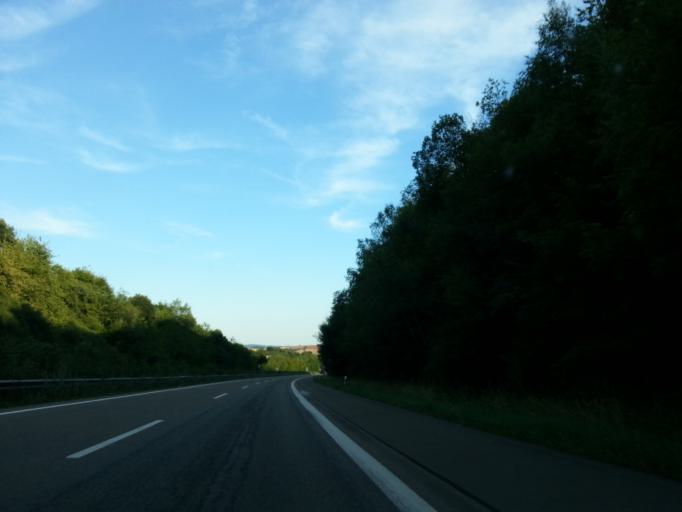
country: DE
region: Rheinland-Pfalz
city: Rehweiler
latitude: 49.4866
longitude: 7.4131
